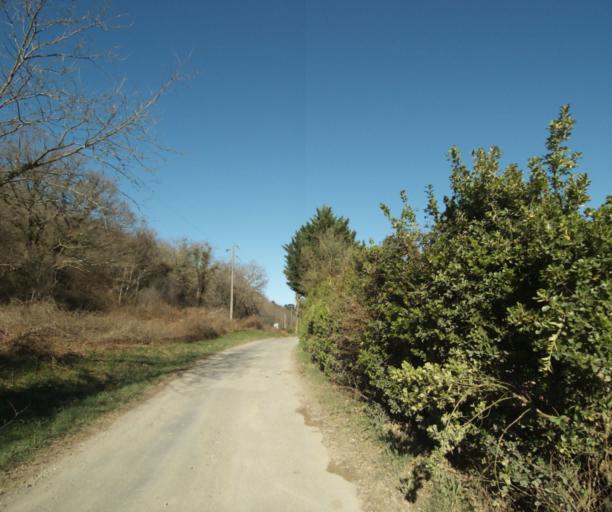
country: FR
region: Aquitaine
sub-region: Departement des Pyrenees-Atlantiques
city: Urrugne
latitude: 43.3604
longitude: -1.7359
